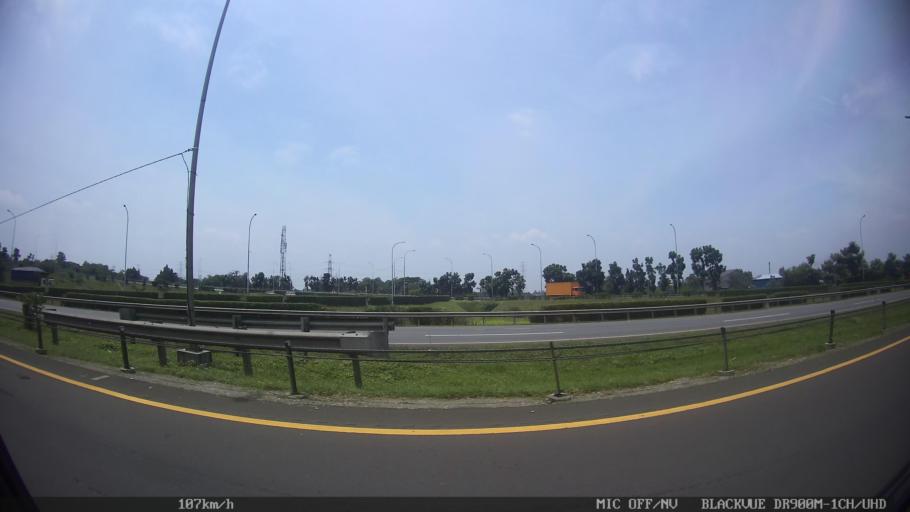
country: ID
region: West Java
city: Kresek
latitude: -6.1733
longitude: 106.3481
